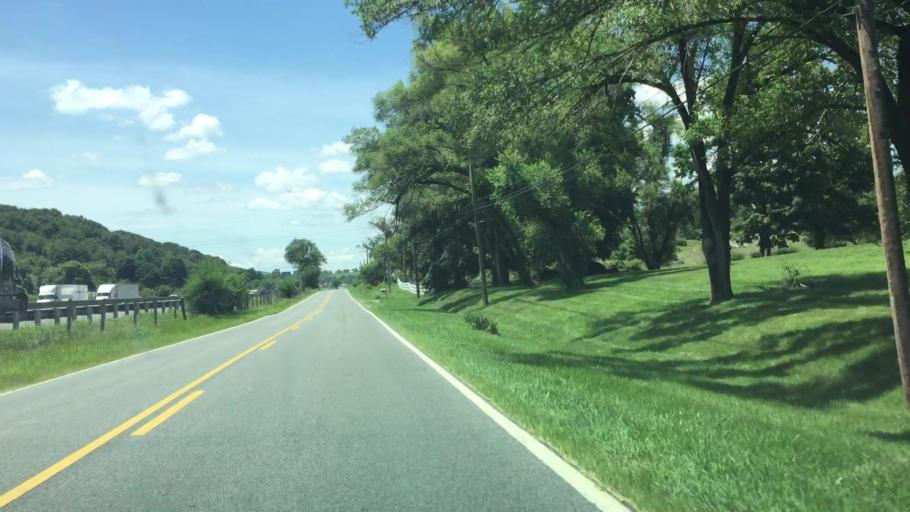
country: US
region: Virginia
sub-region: Wythe County
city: Wytheville
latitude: 36.9450
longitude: -80.9550
